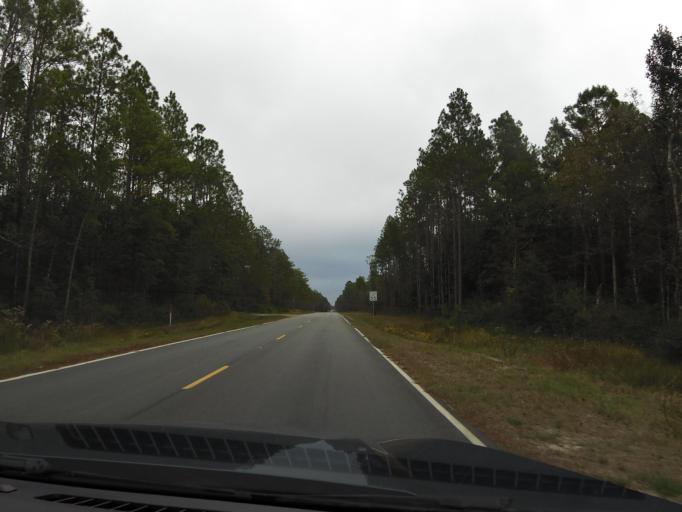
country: US
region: Georgia
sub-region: Charlton County
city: Folkston
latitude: 30.7396
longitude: -82.1038
